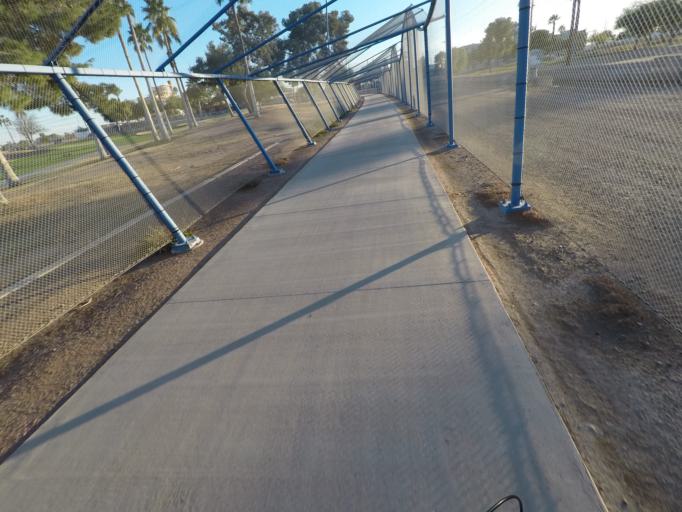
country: US
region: Arizona
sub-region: Maricopa County
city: Guadalupe
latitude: 33.3591
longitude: -111.9378
